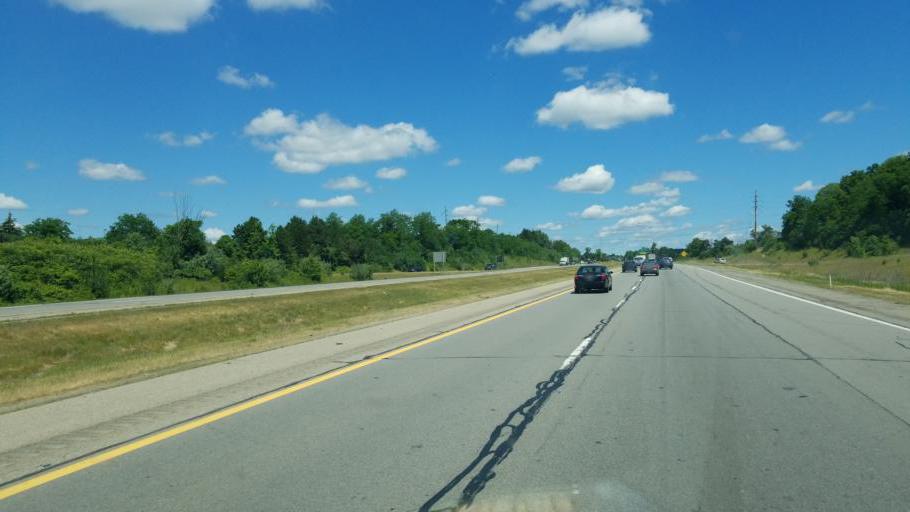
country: US
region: Michigan
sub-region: Washtenaw County
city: Ann Arbor
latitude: 42.3079
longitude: -83.6871
